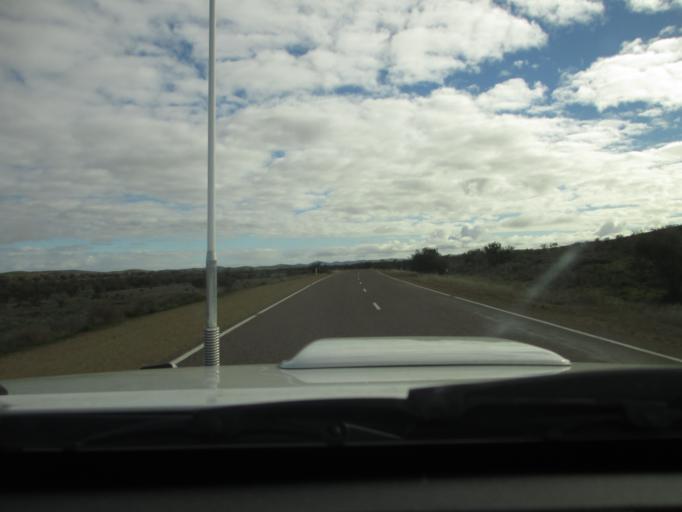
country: AU
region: South Australia
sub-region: Flinders Ranges
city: Quorn
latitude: -32.3591
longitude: 138.4941
